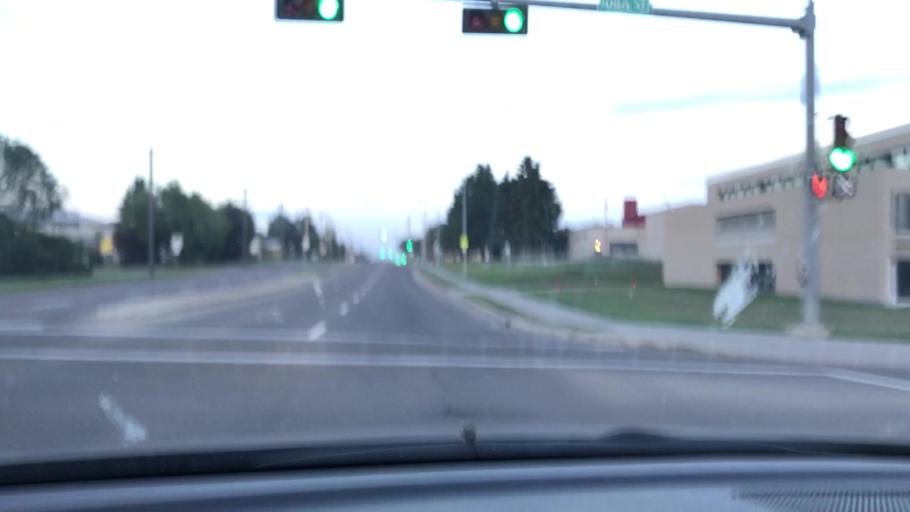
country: CA
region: Alberta
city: Edmonton
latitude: 53.4882
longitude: -113.5110
